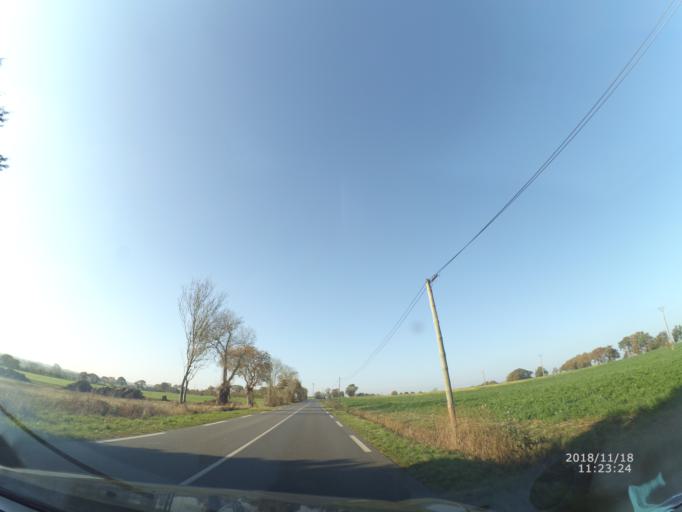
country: FR
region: Pays de la Loire
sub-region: Departement de la Loire-Atlantique
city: Saint-Pere-en-Retz
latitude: 47.2207
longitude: -2.0899
